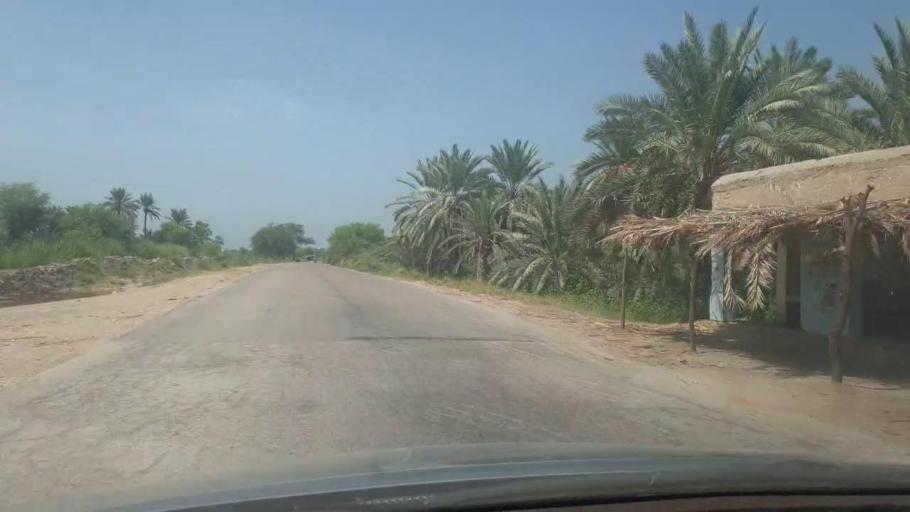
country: PK
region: Sindh
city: Ranipur
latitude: 27.2487
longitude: 68.5810
